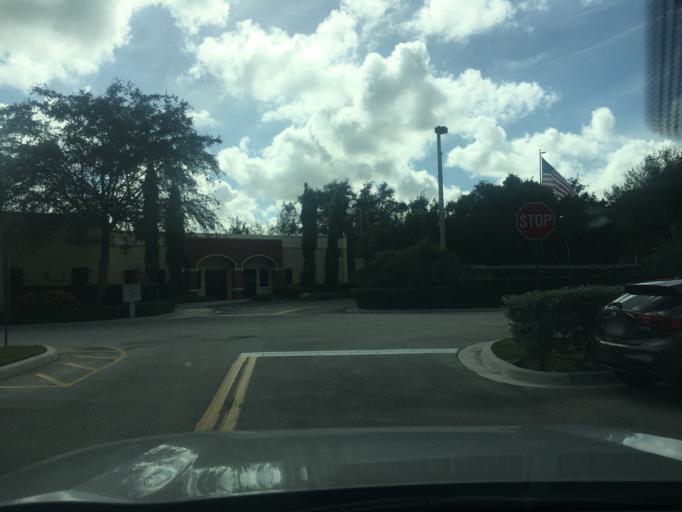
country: US
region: Florida
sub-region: Broward County
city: Broadview Park
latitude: 26.0743
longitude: -80.1810
